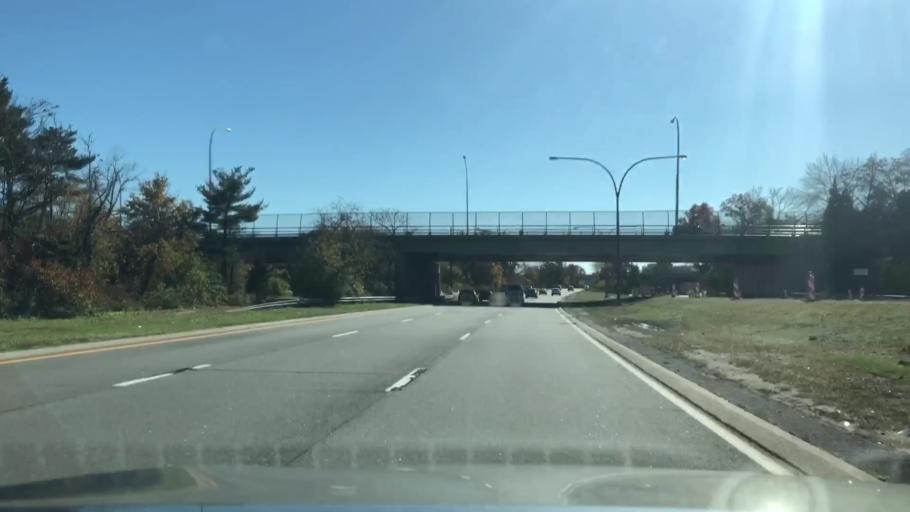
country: US
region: New York
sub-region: Nassau County
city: East Garden City
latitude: 40.7303
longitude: -73.5821
